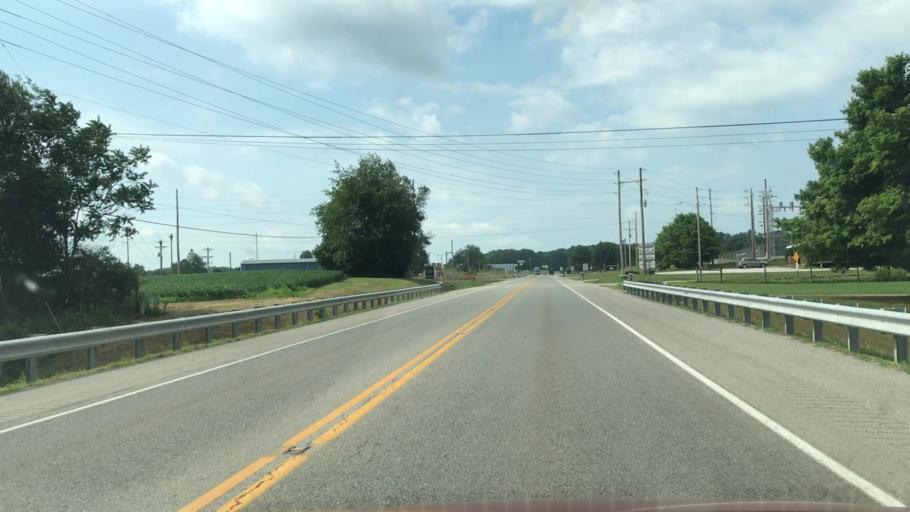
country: US
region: Kentucky
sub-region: Barren County
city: Cave City
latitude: 37.1223
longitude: -85.9620
